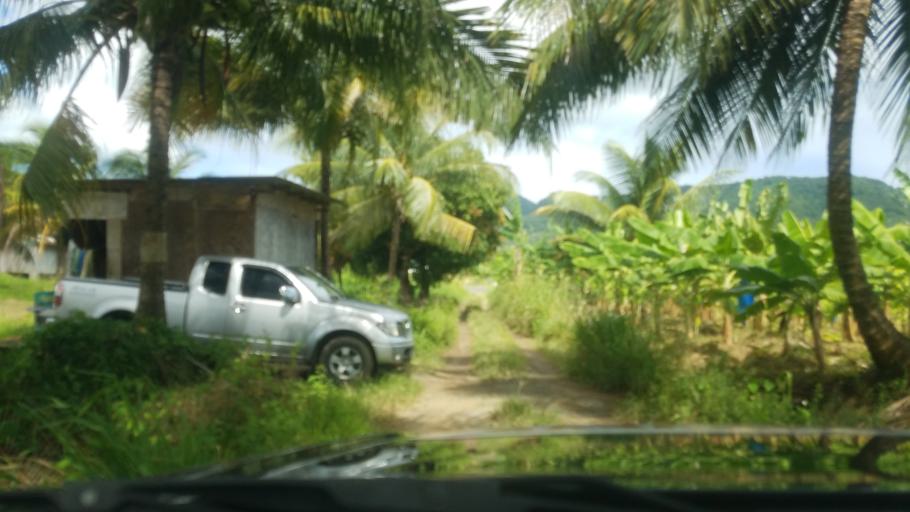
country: LC
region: Dennery Quarter
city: Dennery
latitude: 13.9363
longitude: -60.9177
